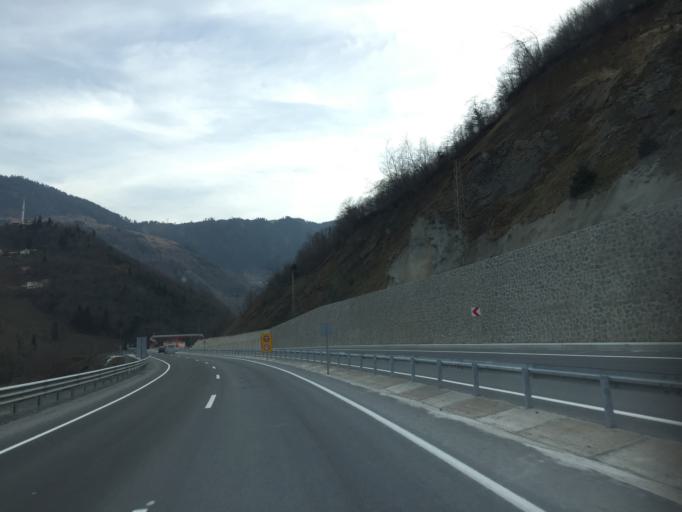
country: TR
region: Trabzon
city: Macka
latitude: 40.7635
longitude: 39.5627
